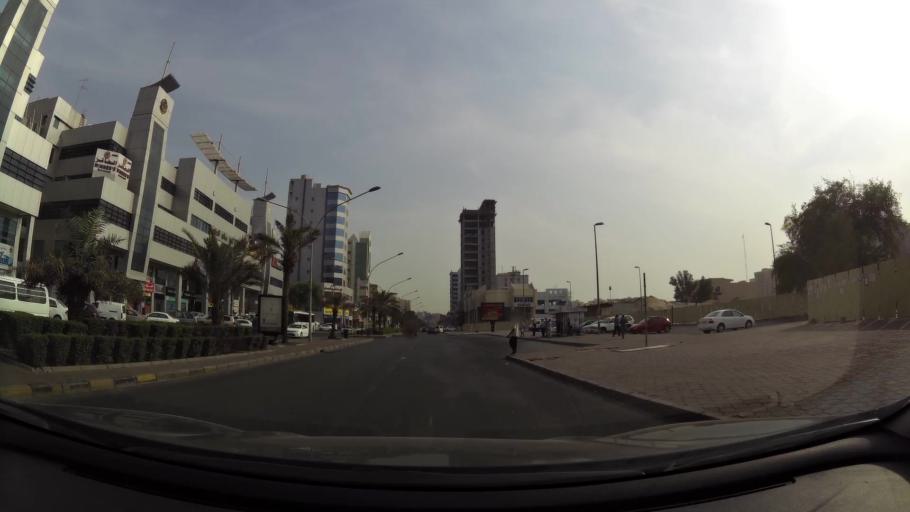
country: KW
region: Al Farwaniyah
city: Al Farwaniyah
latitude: 29.2796
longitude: 47.9613
